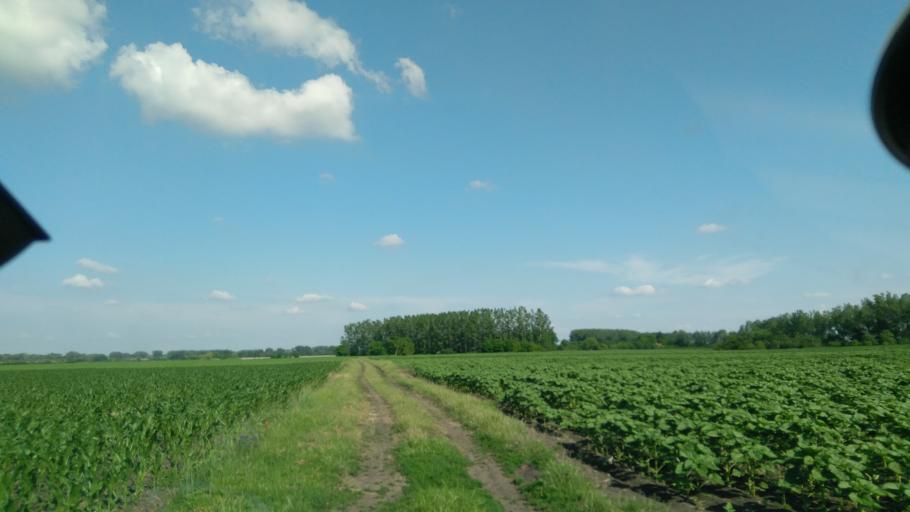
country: HU
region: Bekes
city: Doboz
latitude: 46.7023
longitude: 21.2344
